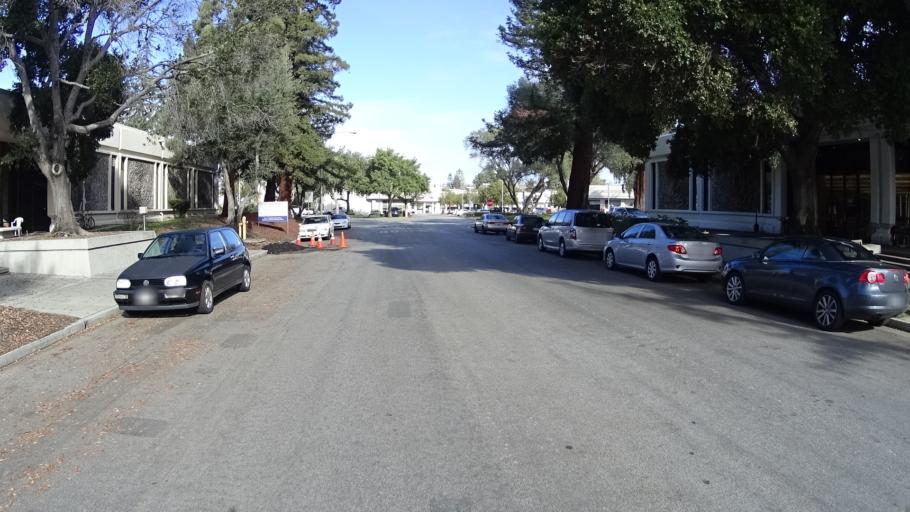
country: US
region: California
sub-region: Santa Clara County
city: Sunnyvale
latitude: 37.3748
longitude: -122.0150
